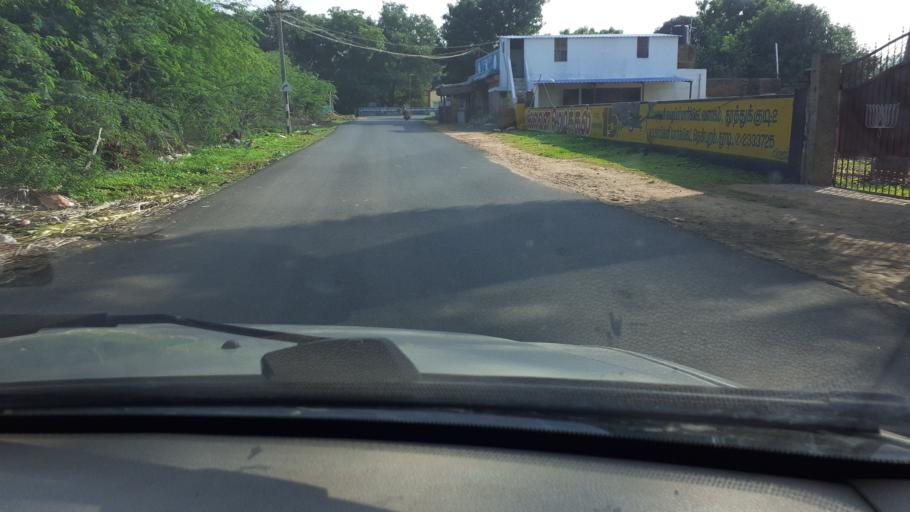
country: IN
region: Tamil Nadu
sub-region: Thoothukkudi
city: Eral
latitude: 8.5789
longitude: 78.0294
